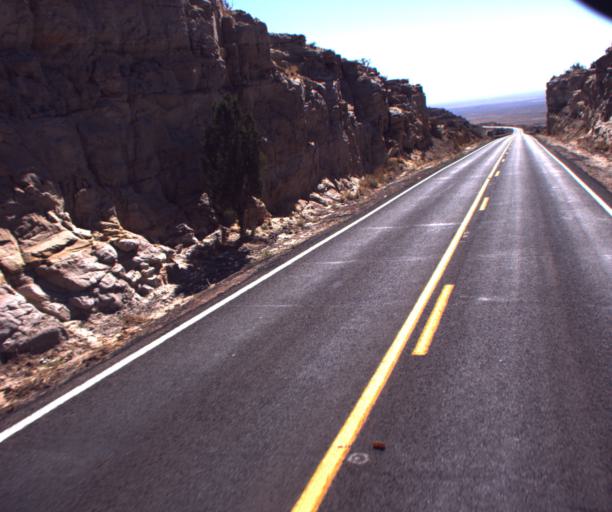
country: US
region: Arizona
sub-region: Navajo County
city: First Mesa
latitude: 35.9018
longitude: -110.6655
